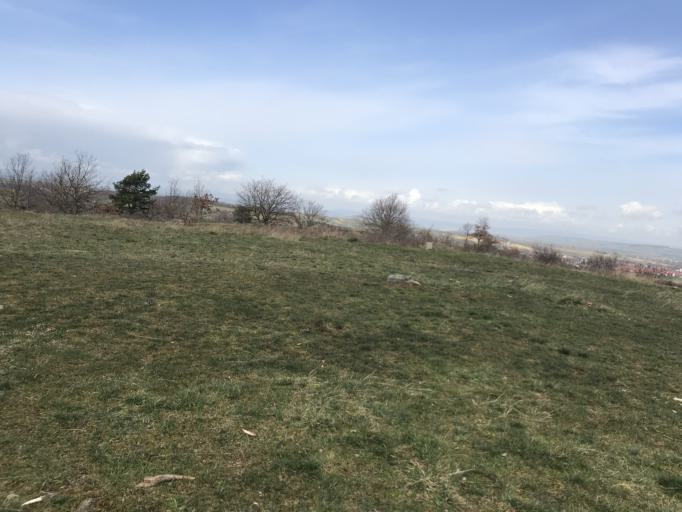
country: DE
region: Rheinland-Pfalz
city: Siefersheim
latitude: 49.7903
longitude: 7.9559
